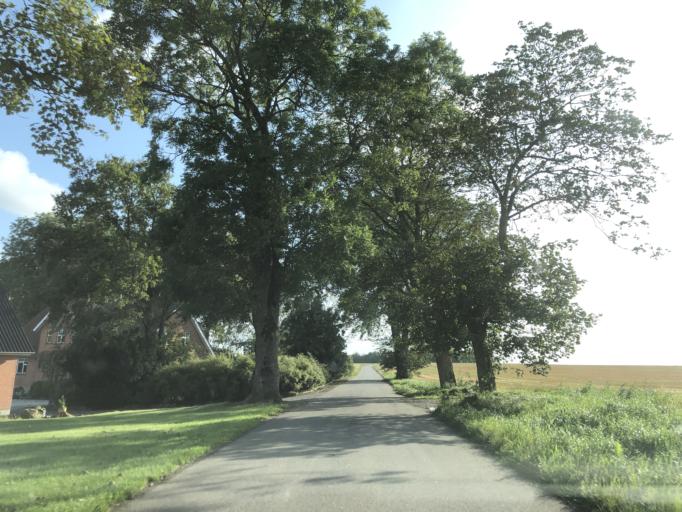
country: DK
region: Central Jutland
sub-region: Favrskov Kommune
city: Hammel
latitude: 56.2395
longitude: 9.7599
